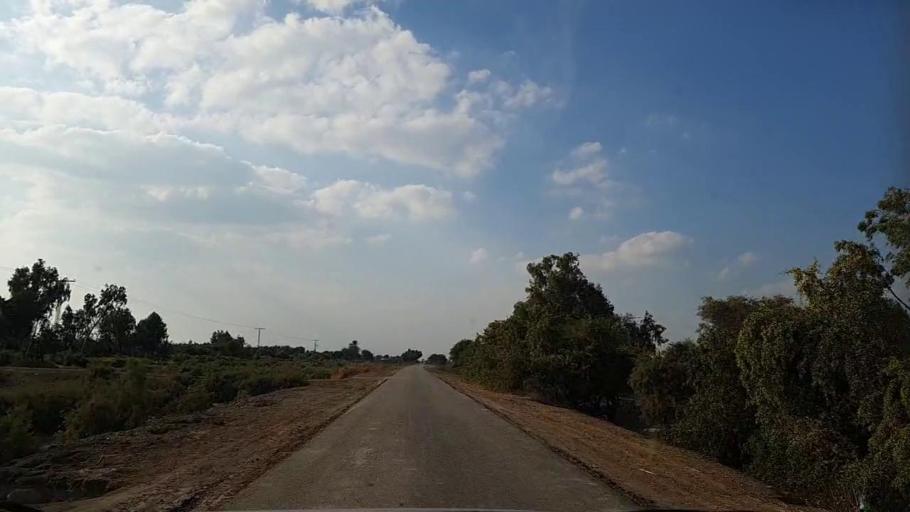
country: PK
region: Sindh
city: Pithoro
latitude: 25.6700
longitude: 69.2296
